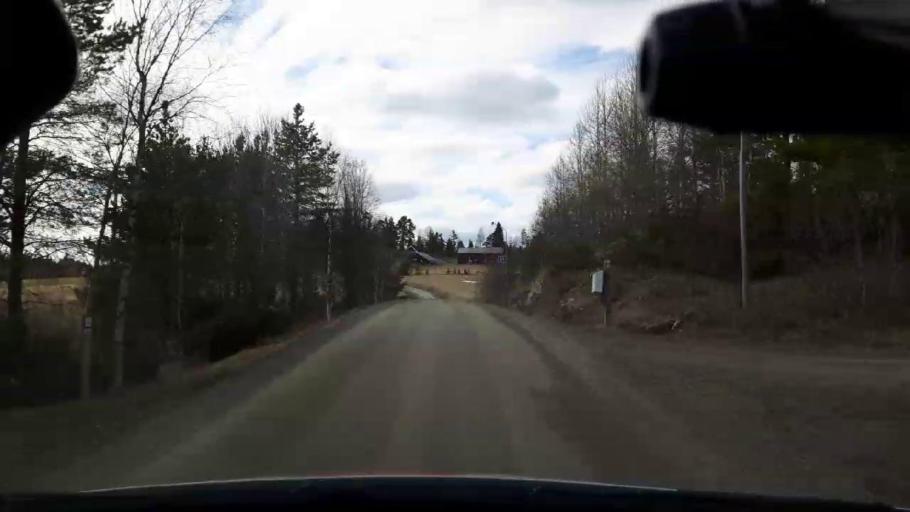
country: SE
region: Jaemtland
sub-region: Bergs Kommun
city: Hoverberg
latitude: 62.8816
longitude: 14.6660
